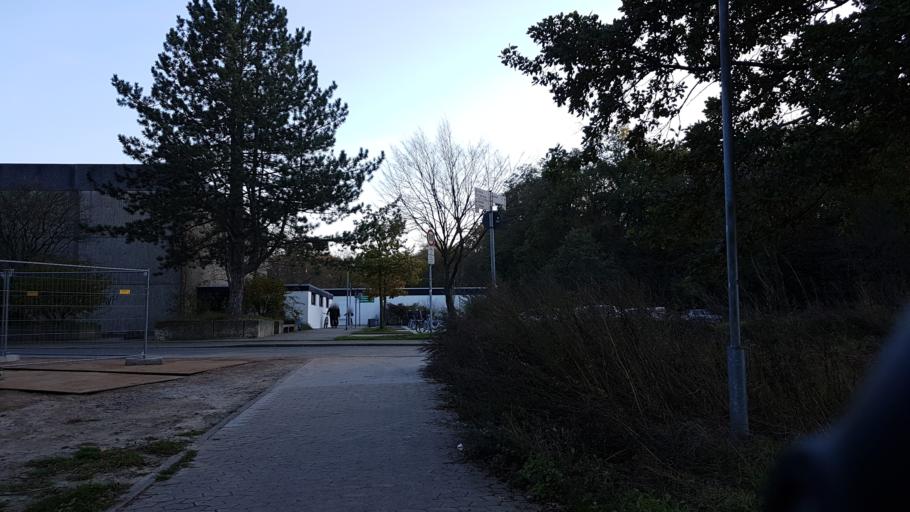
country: DE
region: Lower Saxony
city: Hemmingen
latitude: 52.3239
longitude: 9.6993
